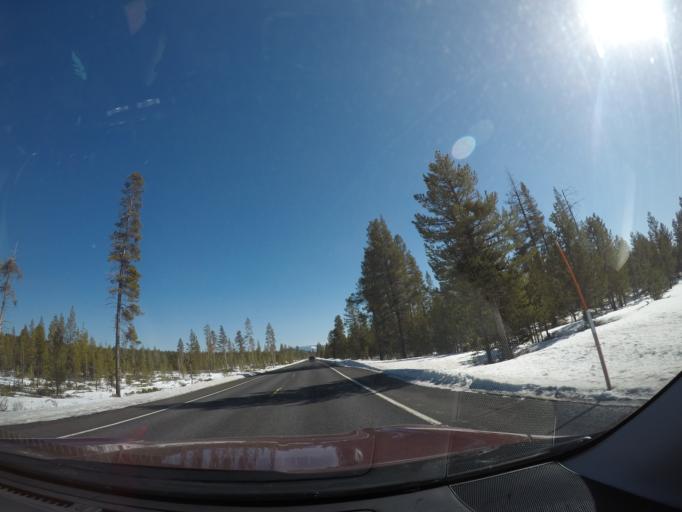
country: US
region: Oregon
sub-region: Deschutes County
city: Three Rivers
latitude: 43.8654
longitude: -121.5394
